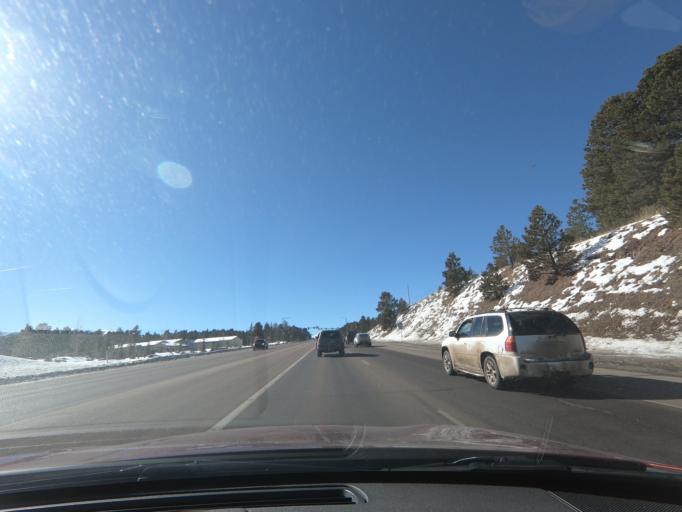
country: US
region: Colorado
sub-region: Teller County
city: Woodland Park
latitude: 38.9764
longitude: -105.0753
